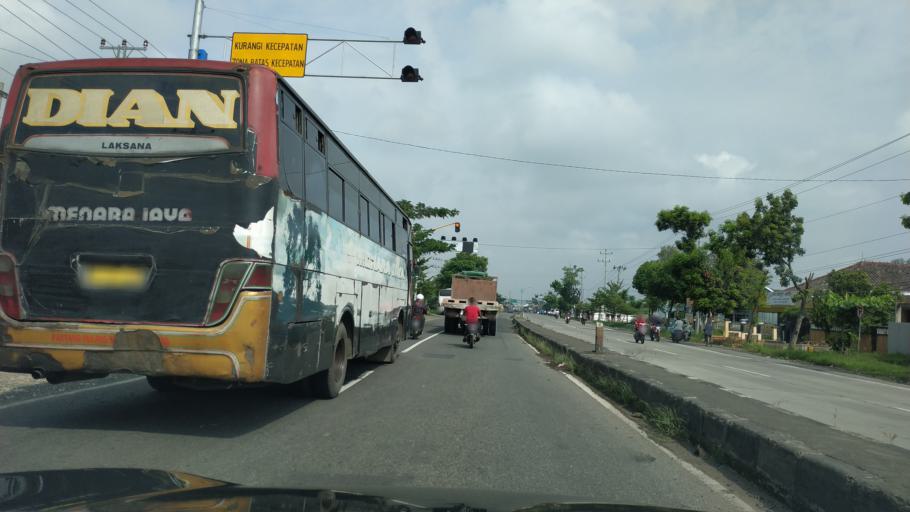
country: ID
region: Central Java
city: Bulakamba
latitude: -6.8750
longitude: 108.9298
